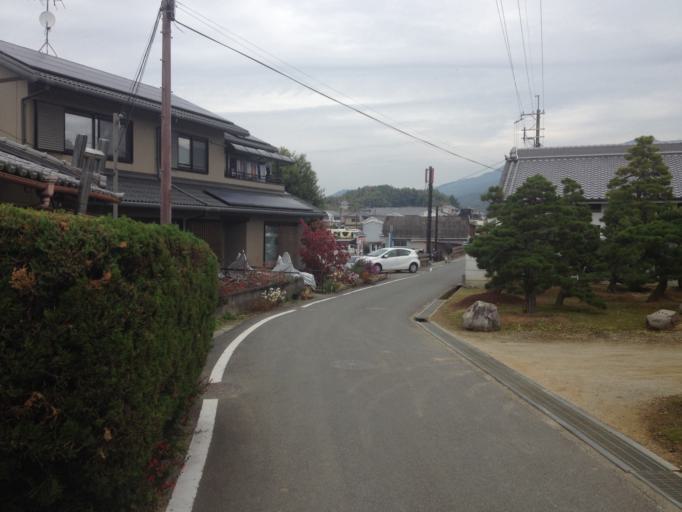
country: JP
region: Nara
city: Kashihara-shi
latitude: 34.4704
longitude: 135.8075
